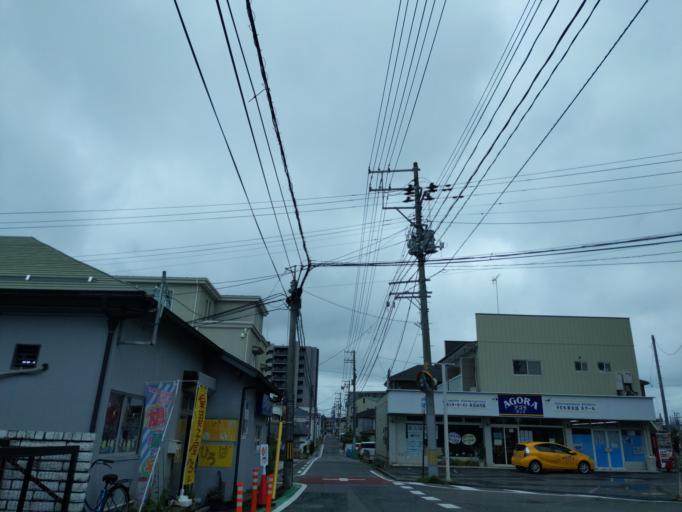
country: JP
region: Fukushima
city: Koriyama
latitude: 37.4039
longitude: 140.3707
